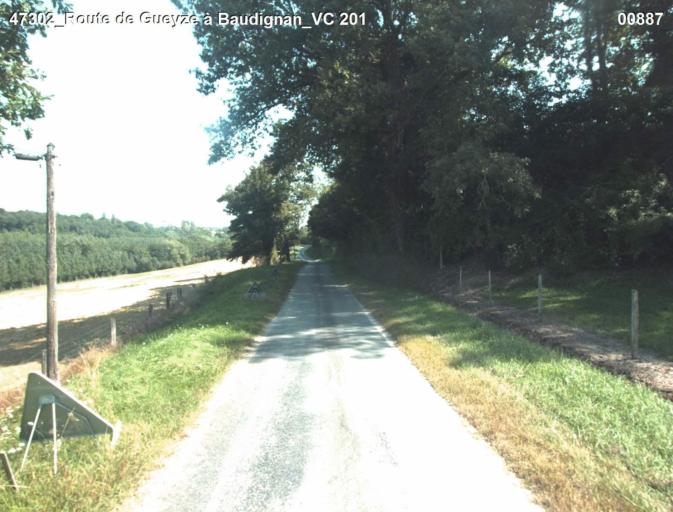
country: FR
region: Midi-Pyrenees
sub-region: Departement du Gers
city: Montreal
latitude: 44.0498
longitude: 0.1235
